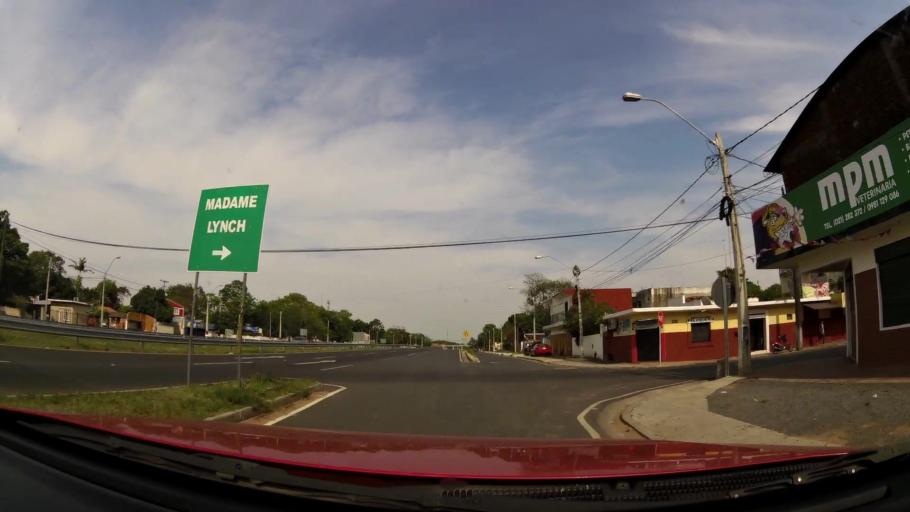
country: PY
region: Central
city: Fernando de la Mora
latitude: -25.2564
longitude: -57.5534
